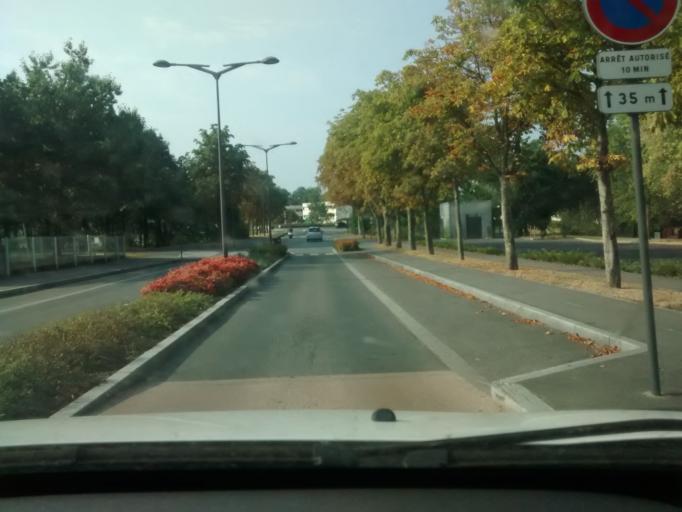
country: FR
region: Brittany
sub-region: Departement d'Ille-et-Vilaine
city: Cesson-Sevigne
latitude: 48.1158
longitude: -1.6007
